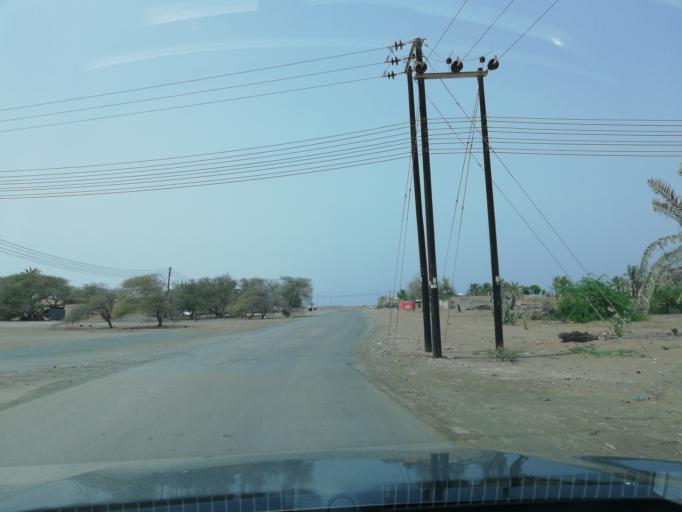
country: OM
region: Al Batinah
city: Al Liwa'
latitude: 24.6176
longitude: 56.5345
